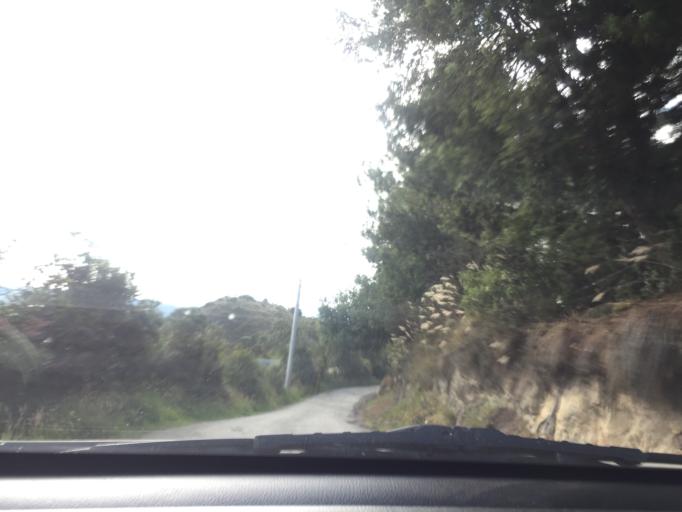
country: CO
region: Cundinamarca
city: Sopo
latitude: 4.9165
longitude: -73.9204
